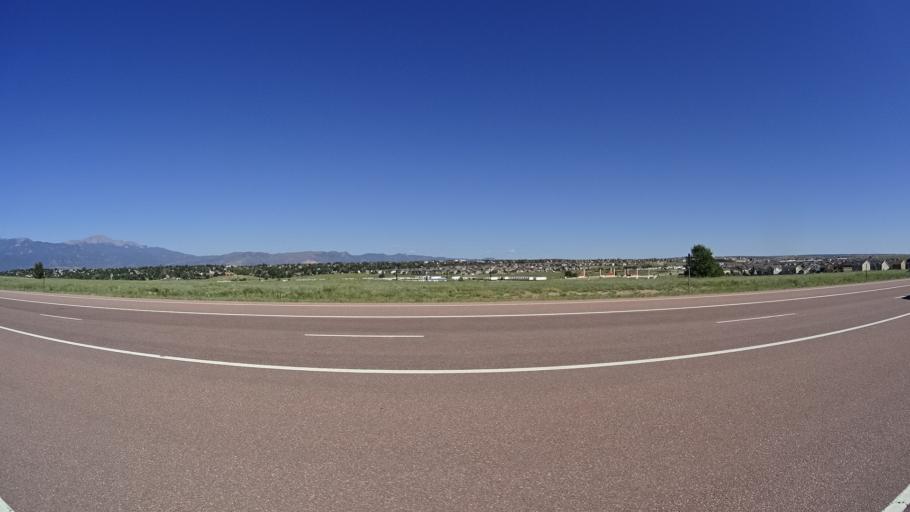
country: US
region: Colorado
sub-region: El Paso County
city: Cimarron Hills
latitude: 38.8533
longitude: -104.6804
